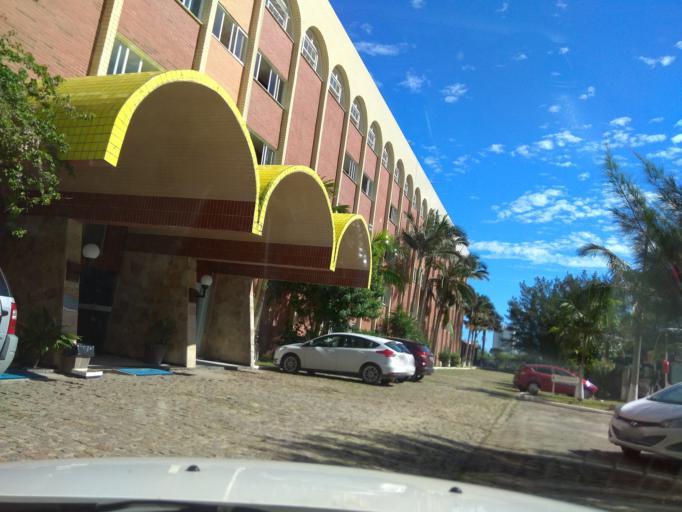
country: BR
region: Santa Catarina
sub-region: Laguna
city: Laguna
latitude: -28.4889
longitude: -48.7663
